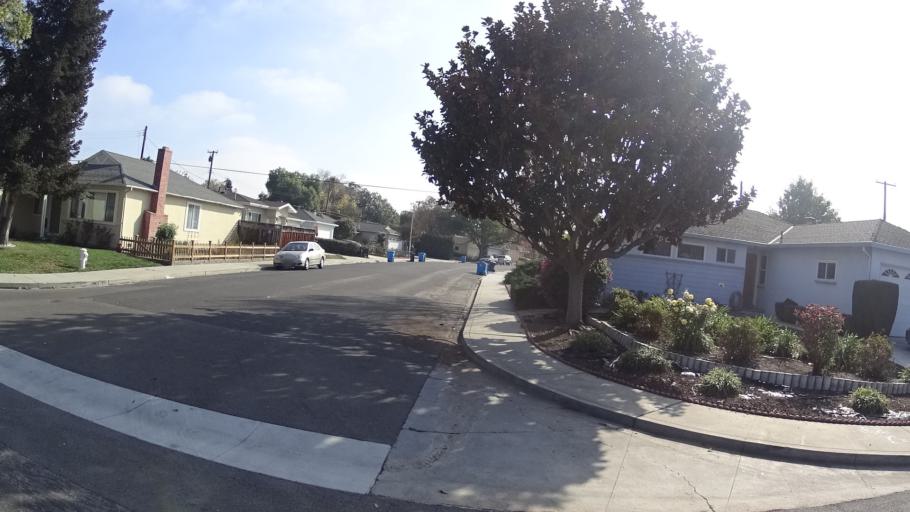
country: US
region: California
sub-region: Santa Clara County
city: Santa Clara
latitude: 37.3560
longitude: -121.9878
